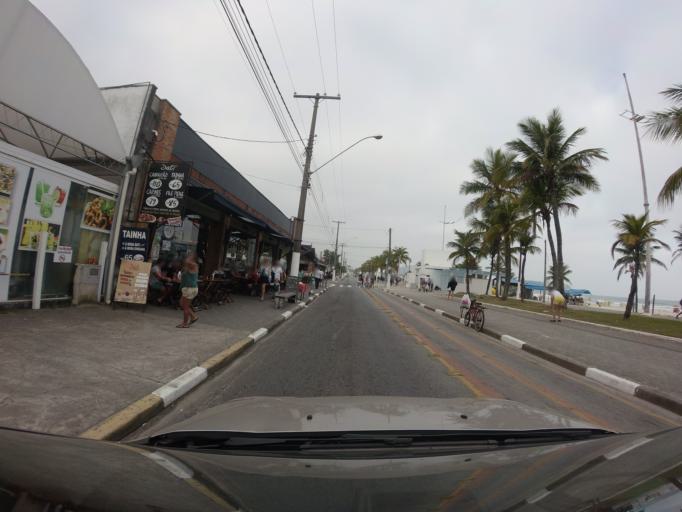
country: BR
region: Sao Paulo
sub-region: Guaruja
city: Guaruja
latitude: -23.9875
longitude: -46.2334
